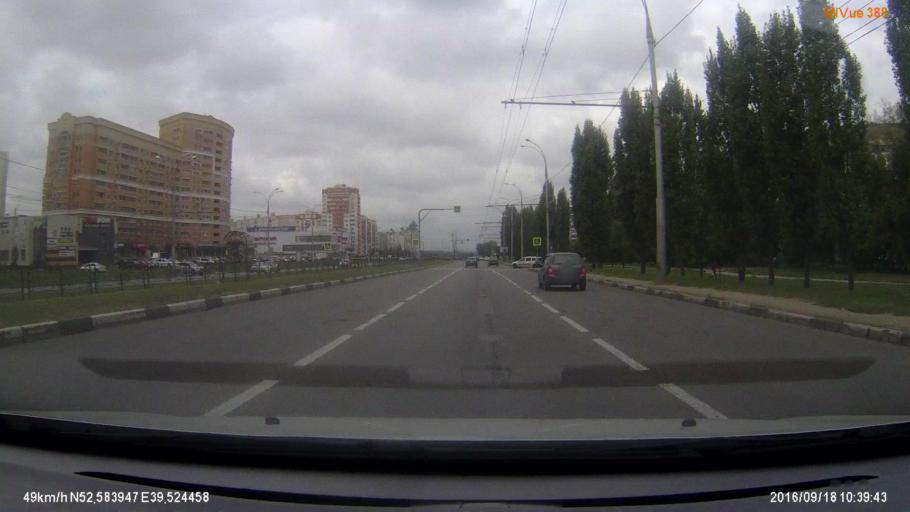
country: RU
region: Lipetsk
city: Syrskoye
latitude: 52.5842
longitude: 39.5239
